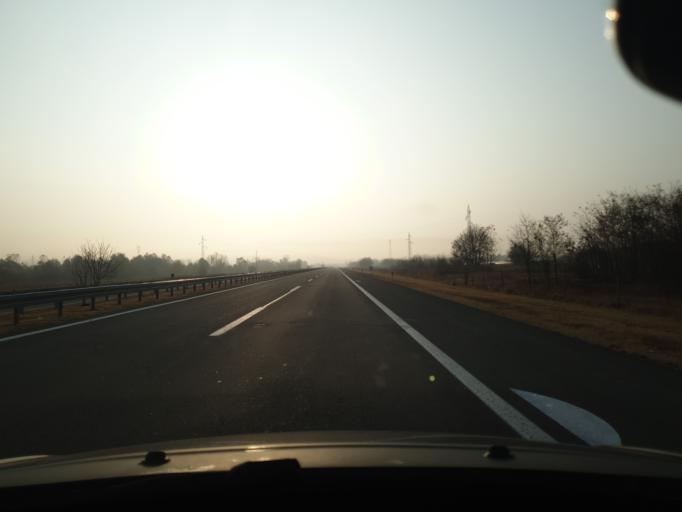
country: RS
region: Central Serbia
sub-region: Jablanicki Okrug
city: Leskovac
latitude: 43.0272
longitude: 22.0088
